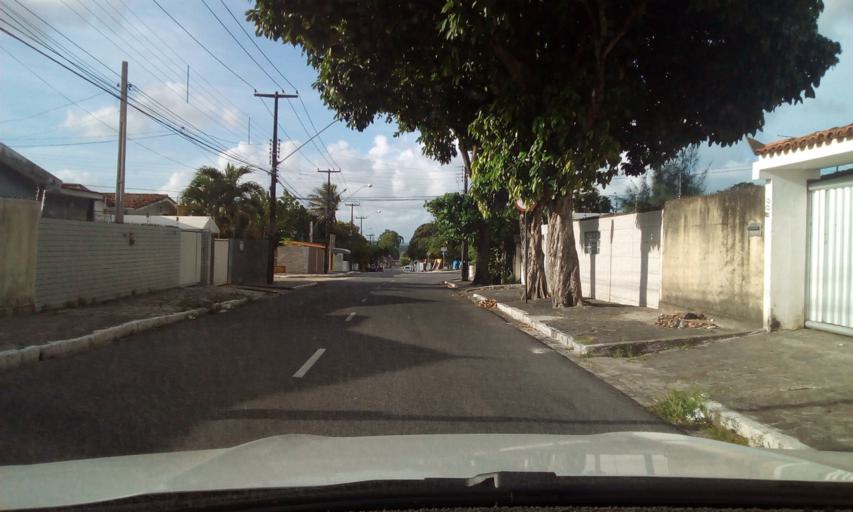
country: BR
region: Paraiba
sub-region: Joao Pessoa
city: Joao Pessoa
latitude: -7.1054
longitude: -34.8556
